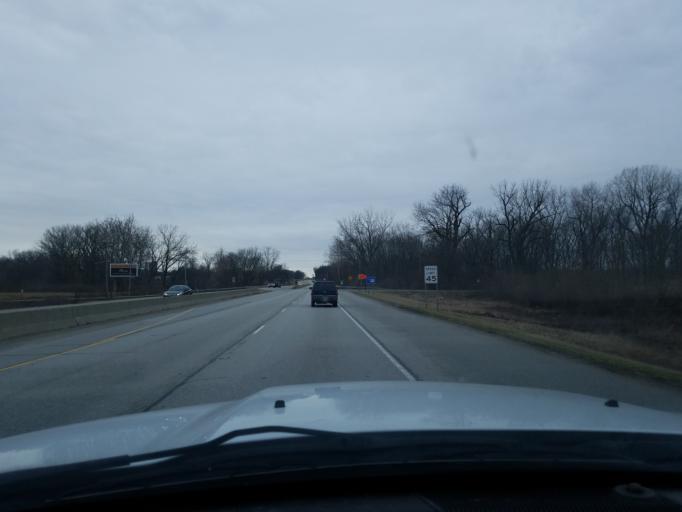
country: US
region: Indiana
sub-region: Tippecanoe County
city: Lafayette
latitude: 40.4549
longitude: -86.8495
